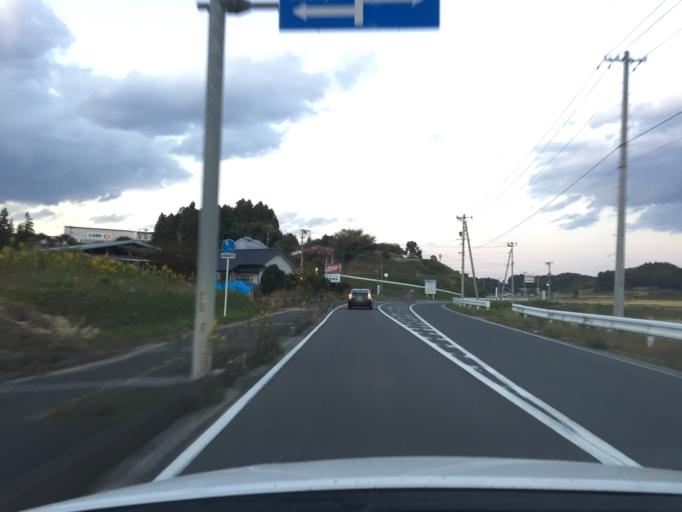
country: JP
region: Fukushima
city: Motomiya
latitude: 37.4924
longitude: 140.4523
